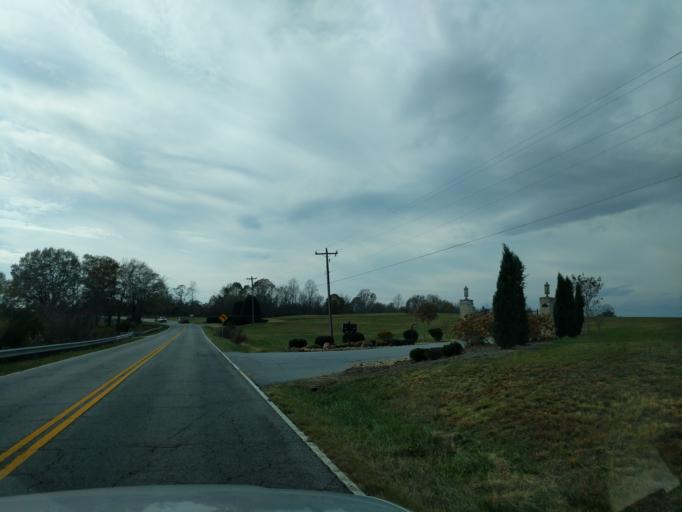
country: US
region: South Carolina
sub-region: Pickens County
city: Central
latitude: 34.8411
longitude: -82.8254
